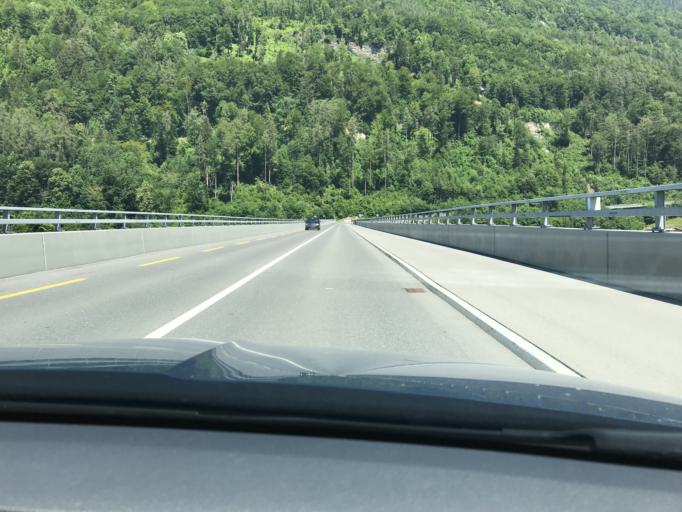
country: CH
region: Bern
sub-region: Interlaken-Oberhasli District
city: Interlaken
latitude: 46.6919
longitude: 7.8723
